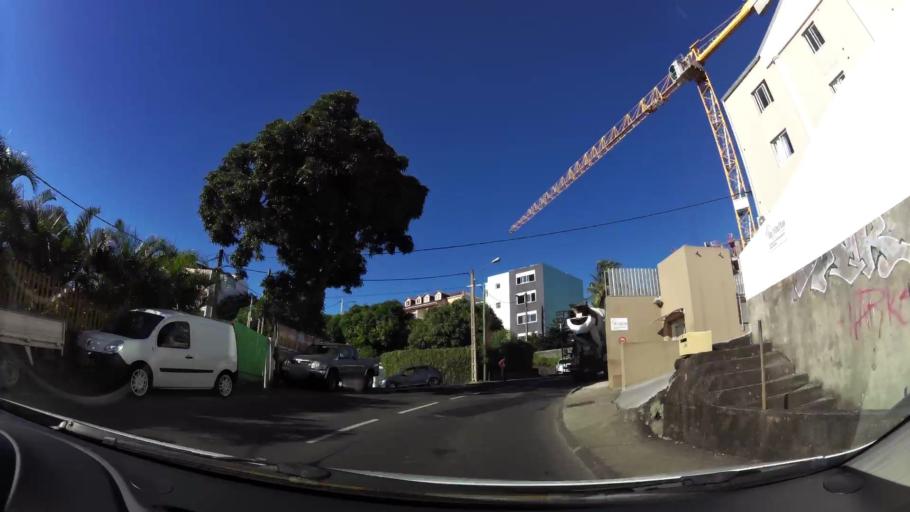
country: RE
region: Reunion
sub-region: Reunion
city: Saint-Denis
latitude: -20.9012
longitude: 55.4767
